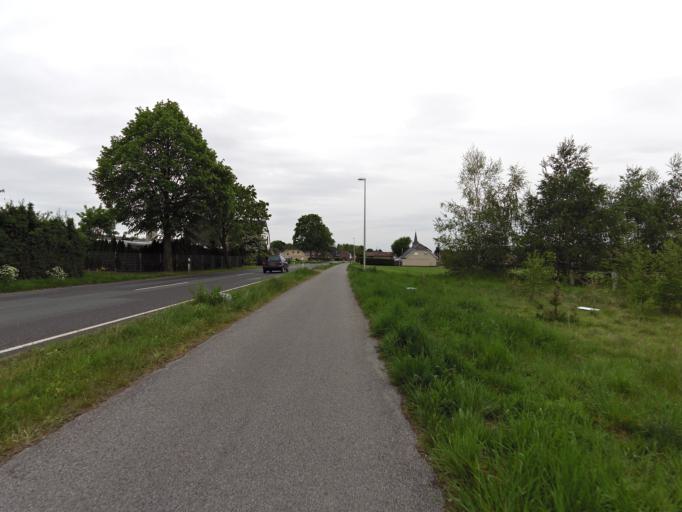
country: DE
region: North Rhine-Westphalia
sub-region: Regierungsbezirk Dusseldorf
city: Emmerich
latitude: 51.8761
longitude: 6.1672
